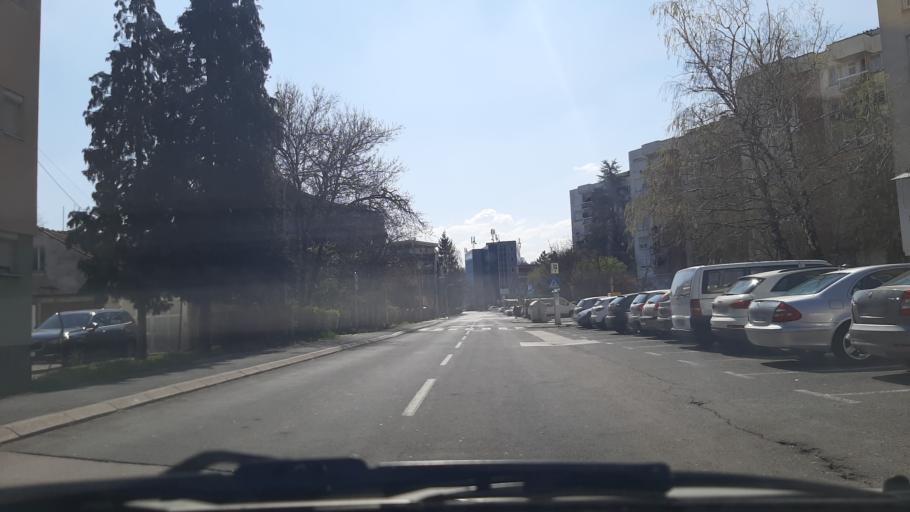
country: BA
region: Republika Srpska
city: Banja Luka
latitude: 44.7738
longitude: 17.1841
